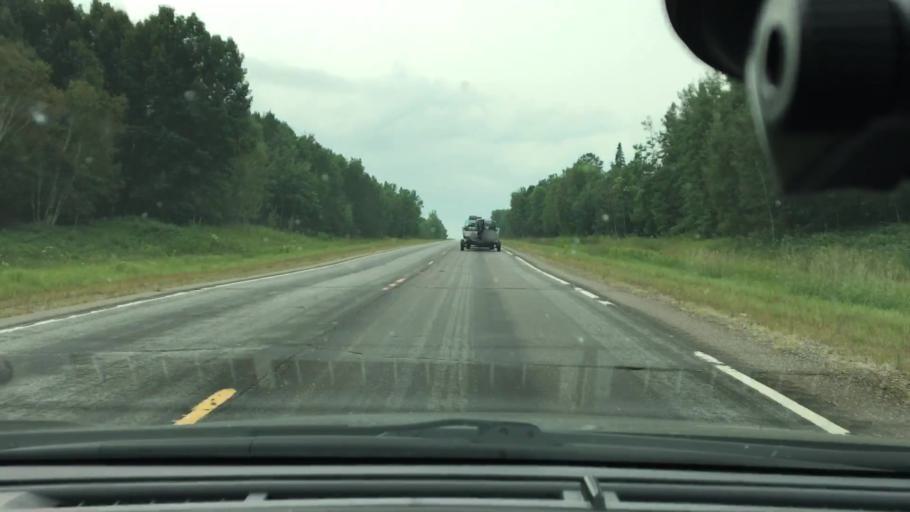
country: US
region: Minnesota
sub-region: Crow Wing County
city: Crosby
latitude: 46.6443
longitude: -93.9518
